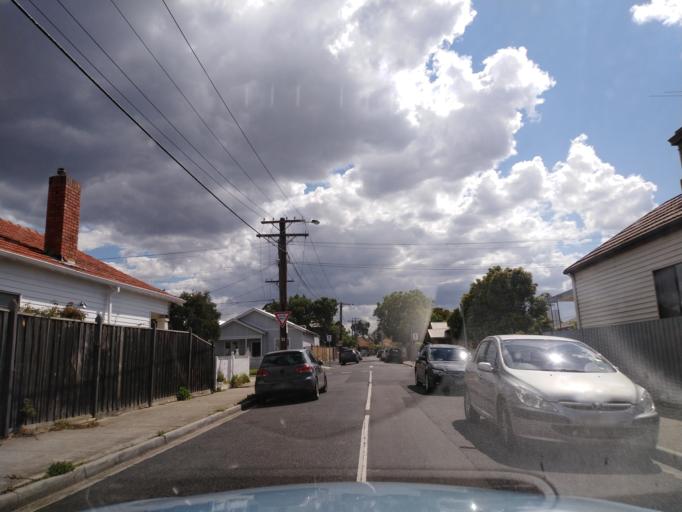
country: AU
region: Victoria
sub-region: Hobsons Bay
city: Newport
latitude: -37.8375
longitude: 144.8802
